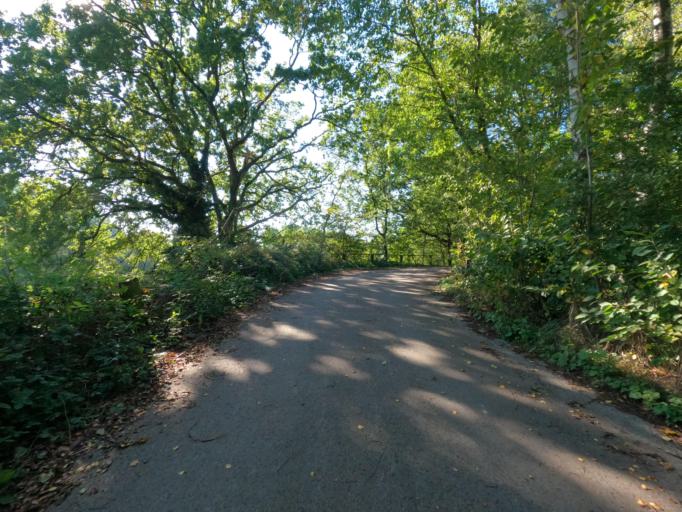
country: DE
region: North Rhine-Westphalia
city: Erkelenz
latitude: 51.0401
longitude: 6.2924
